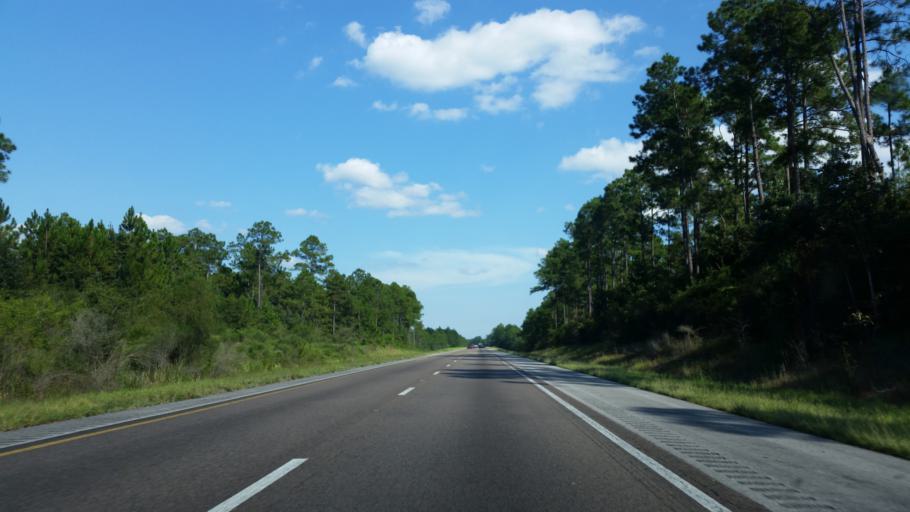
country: US
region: Alabama
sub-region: Baldwin County
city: Robertsdale
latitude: 30.5856
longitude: -87.5311
